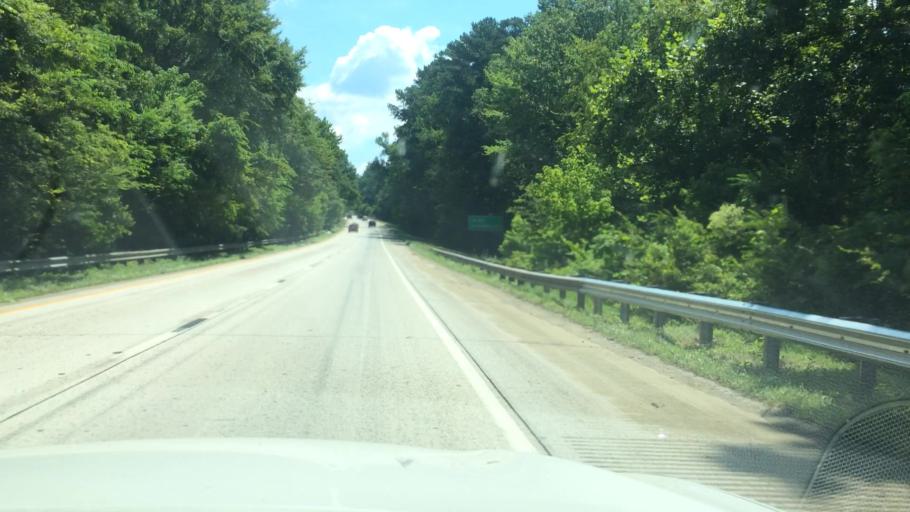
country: US
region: South Carolina
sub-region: Aiken County
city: Belvedere
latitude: 33.5434
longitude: -81.9773
